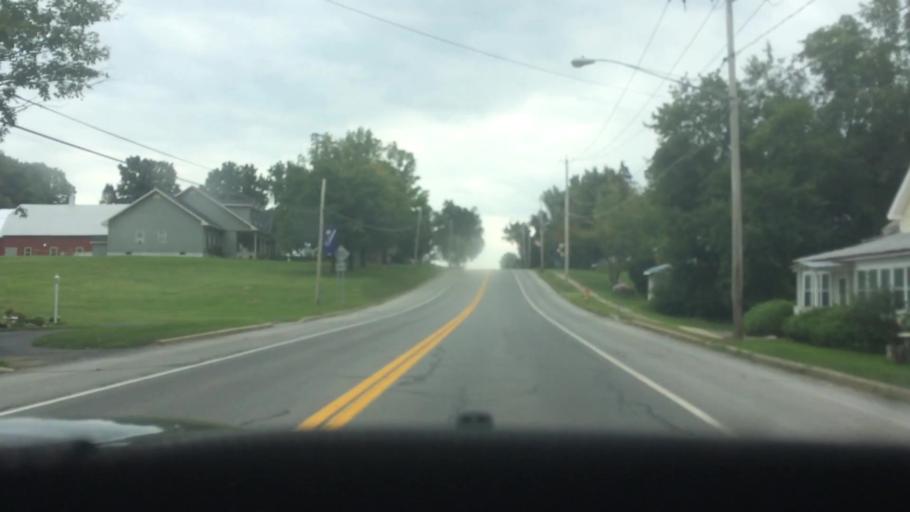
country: US
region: New York
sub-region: St. Lawrence County
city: Ogdensburg
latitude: 44.6149
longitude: -75.4025
